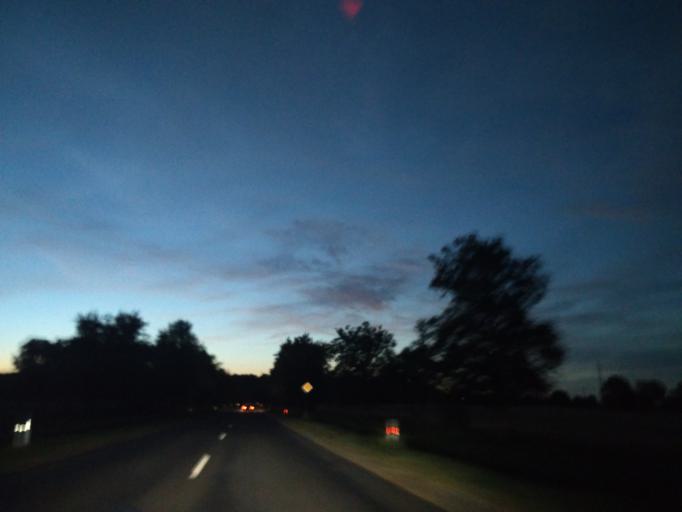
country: HU
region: Vas
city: Vasvar
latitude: 46.9976
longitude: 16.8290
